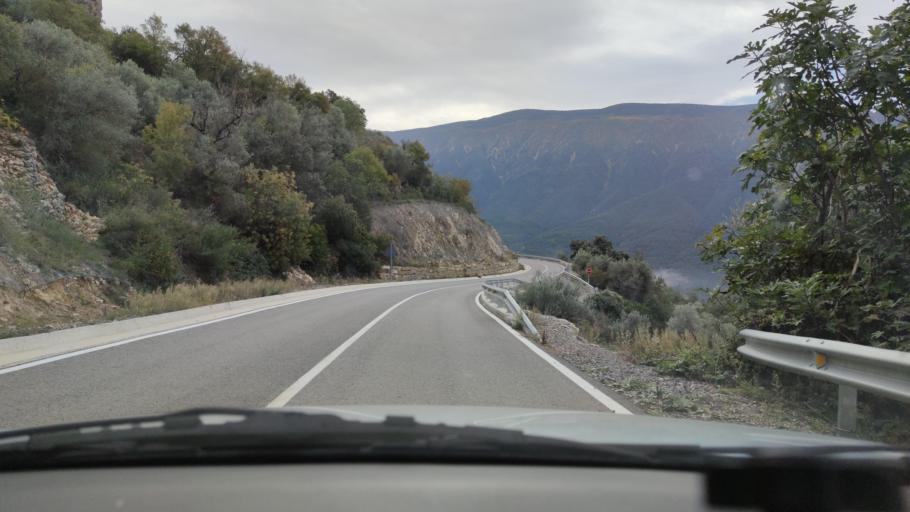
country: ES
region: Catalonia
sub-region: Provincia de Lleida
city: Llimiana
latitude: 42.0715
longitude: 0.9168
